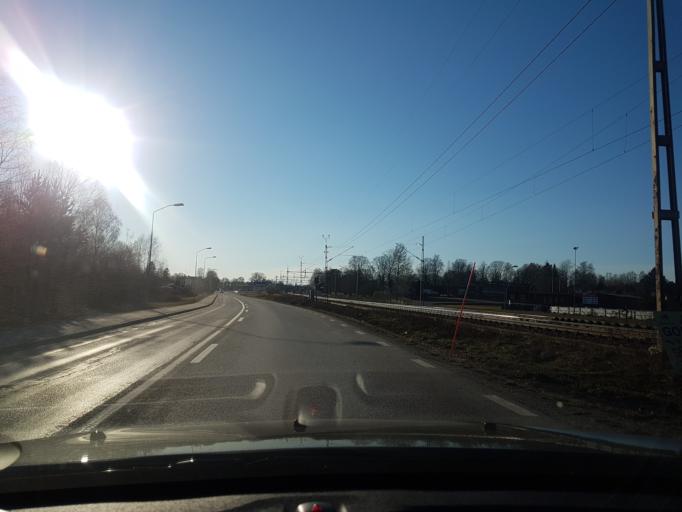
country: SE
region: Uppsala
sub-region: Heby Kommun
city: Morgongava
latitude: 59.9320
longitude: 16.9678
